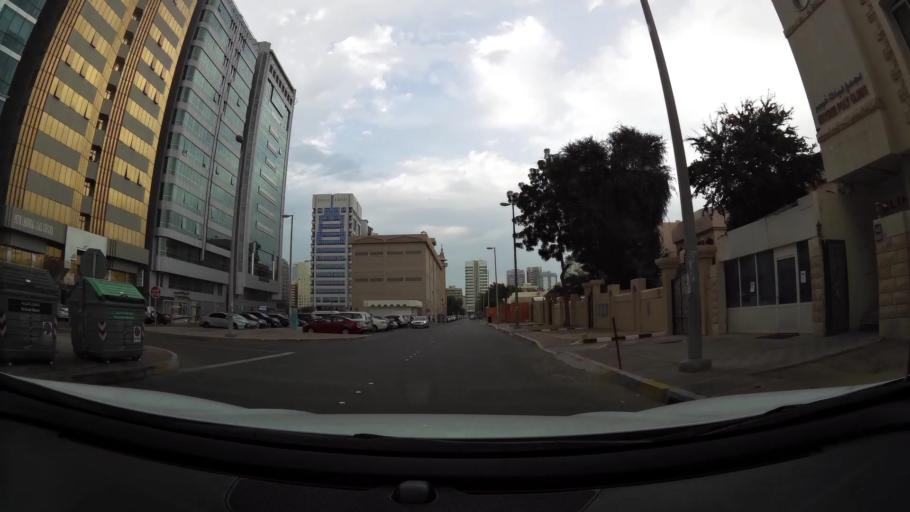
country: AE
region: Abu Dhabi
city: Abu Dhabi
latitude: 24.4758
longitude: 54.3746
